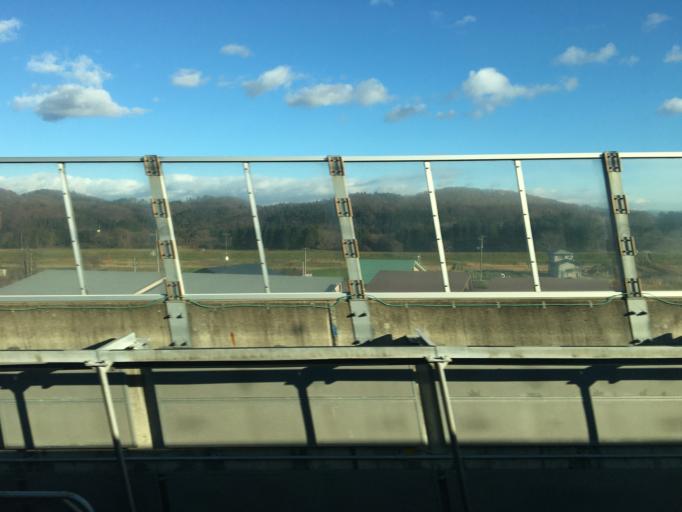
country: JP
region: Iwate
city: Kitakami
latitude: 39.2579
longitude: 141.1125
